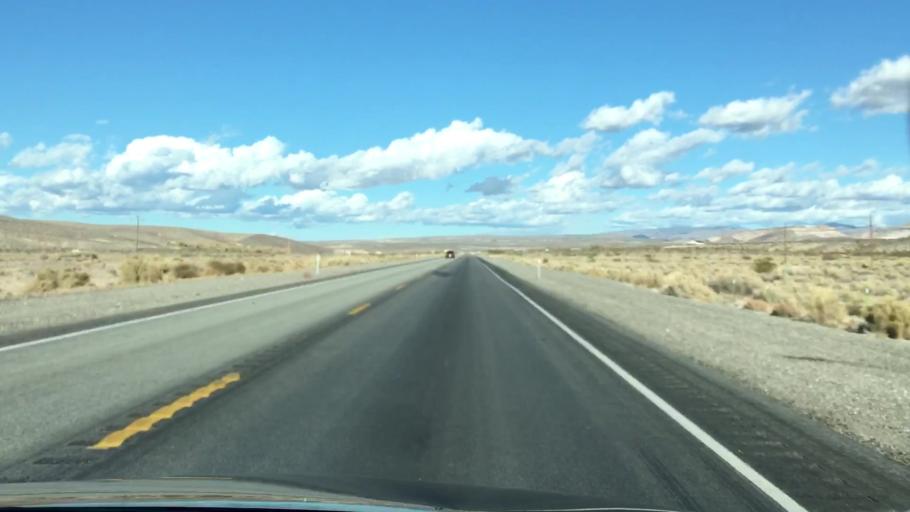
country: US
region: Nevada
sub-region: Nye County
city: Beatty
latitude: 36.9273
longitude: -116.7364
